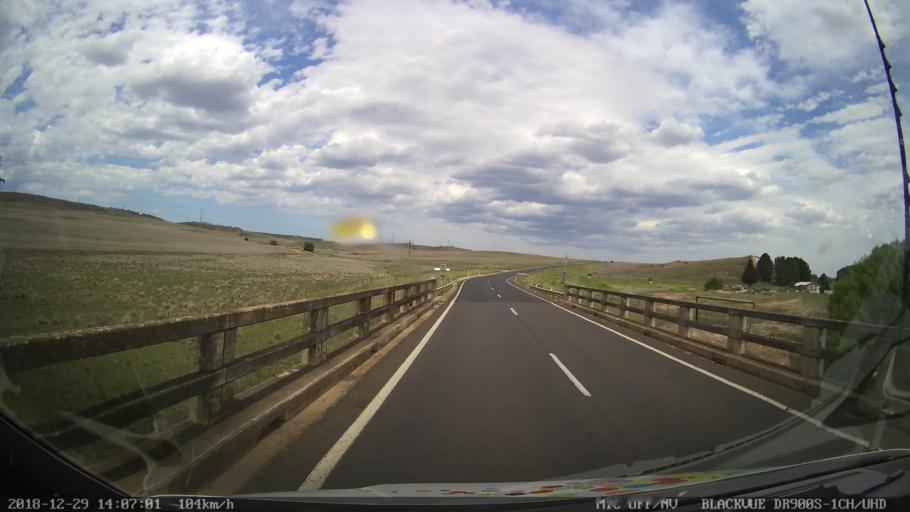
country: AU
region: New South Wales
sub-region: Cooma-Monaro
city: Cooma
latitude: -36.3467
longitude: 149.2100
